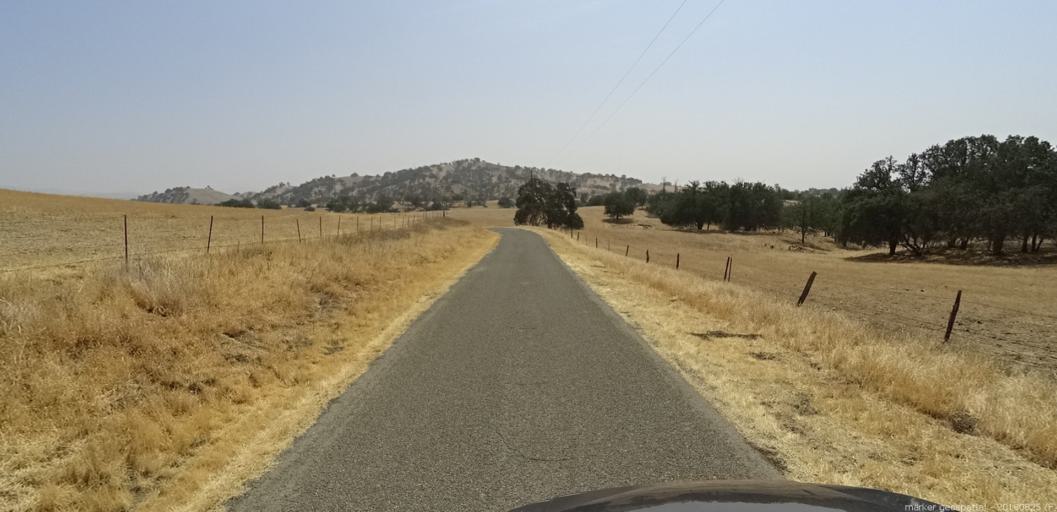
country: US
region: California
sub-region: San Luis Obispo County
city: Shandon
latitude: 35.8757
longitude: -120.3870
